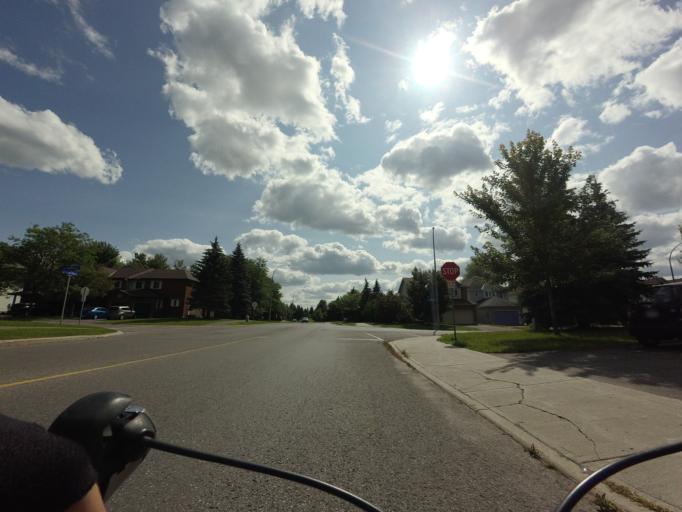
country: CA
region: Ontario
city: Bells Corners
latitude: 45.2934
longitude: -75.8578
